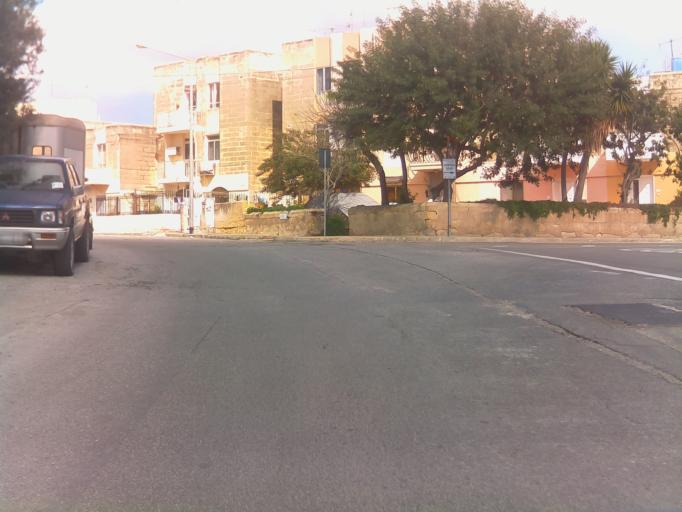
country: MT
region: Saint Lucia
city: Santa Lucija
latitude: 35.8622
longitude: 14.5017
